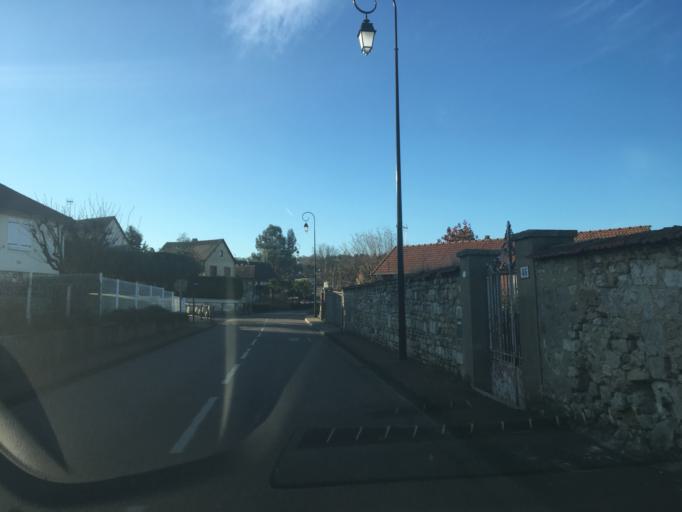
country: FR
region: Haute-Normandie
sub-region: Departement de l'Eure
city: Saint-Marcel
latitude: 49.0952
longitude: 1.4519
